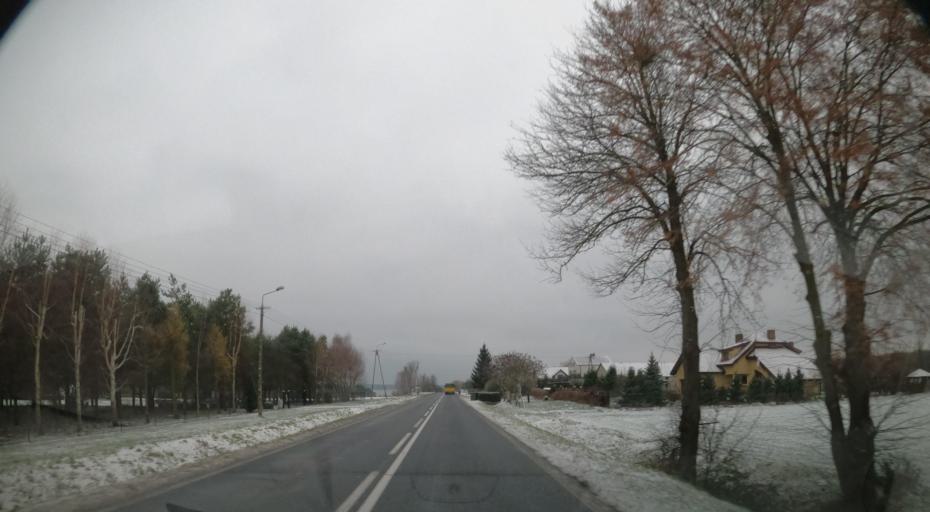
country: PL
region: Masovian Voivodeship
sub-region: Powiat plocki
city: Maszewo Duze
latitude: 52.5710
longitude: 19.5784
